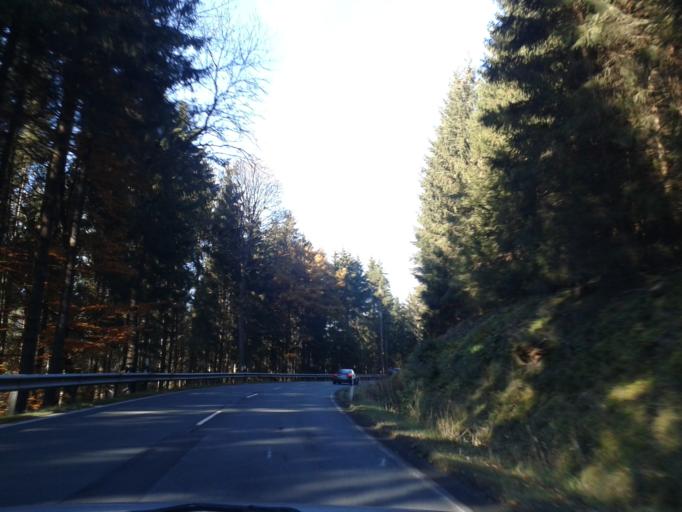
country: DE
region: North Rhine-Westphalia
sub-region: Regierungsbezirk Arnsberg
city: Bad Berleburg
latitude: 51.1000
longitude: 8.4316
